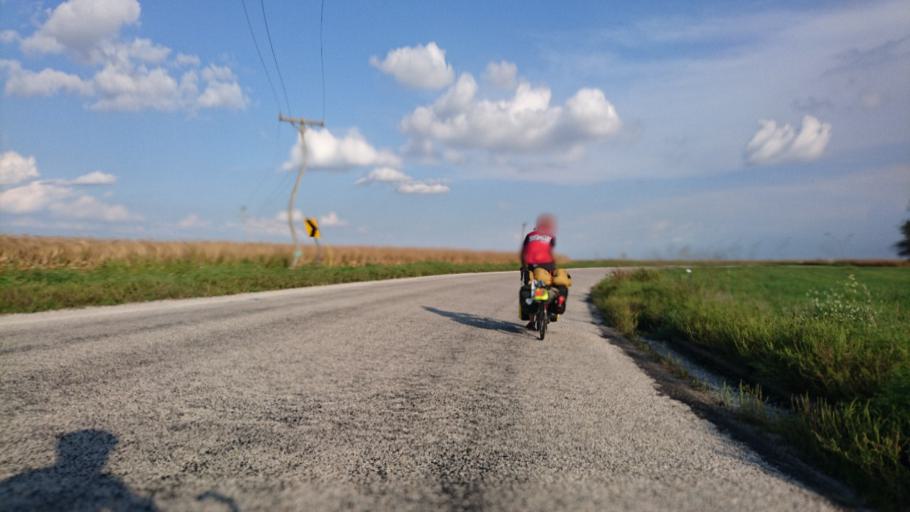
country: US
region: Illinois
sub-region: Logan County
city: Atlanta
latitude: 40.2597
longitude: -89.2065
